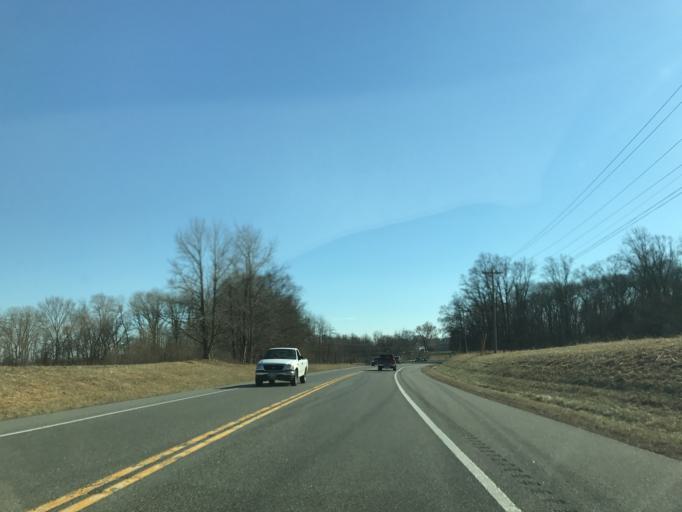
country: US
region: Maryland
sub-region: Queen Anne's County
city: Centreville
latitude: 39.0026
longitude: -76.0737
